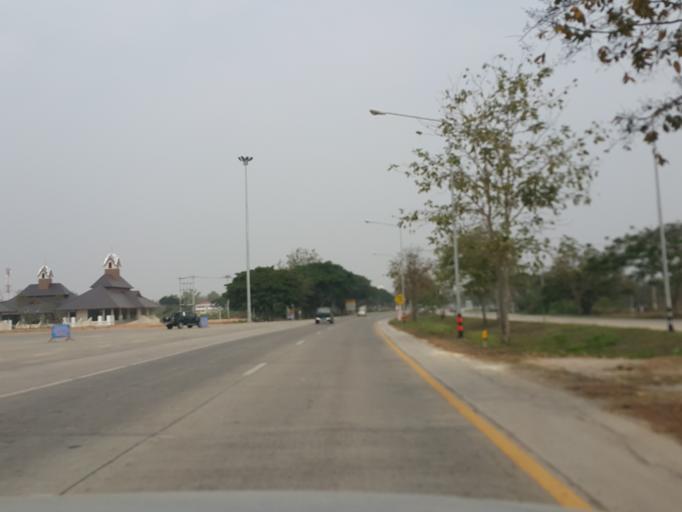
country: TH
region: Lampang
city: Ko Kha
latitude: 18.1934
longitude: 99.4065
